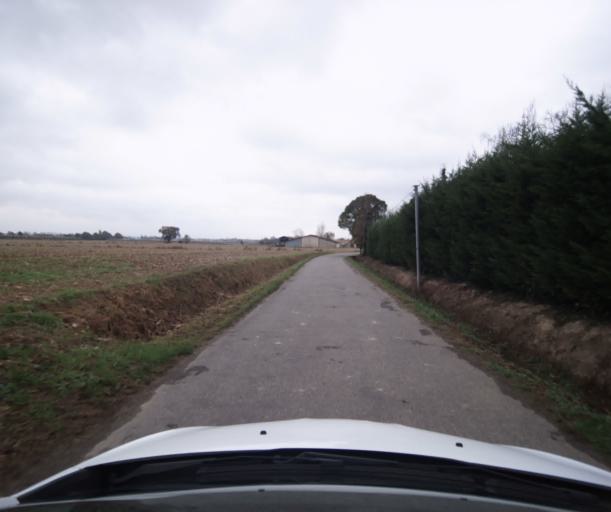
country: FR
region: Midi-Pyrenees
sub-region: Departement du Tarn-et-Garonne
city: Castelsarrasin
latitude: 44.0488
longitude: 1.1346
